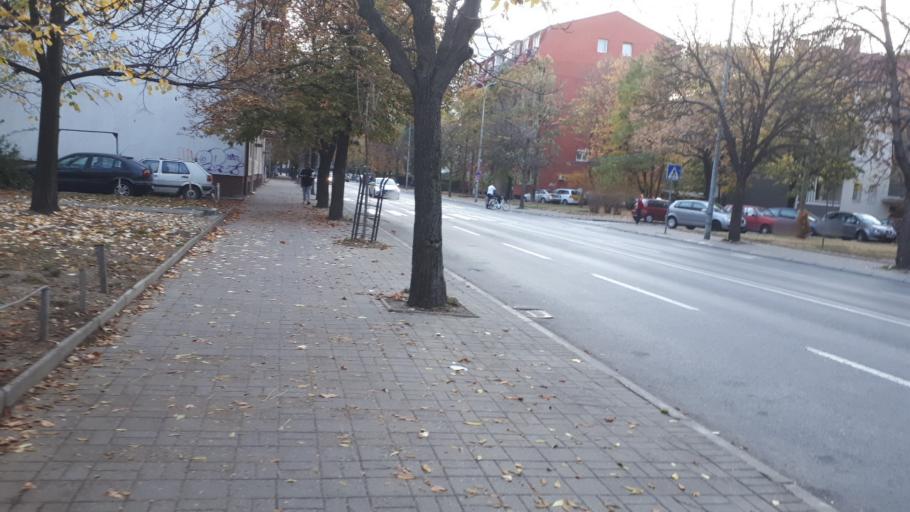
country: MK
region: Karpos
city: Skopje
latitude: 42.0030
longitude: 21.4146
